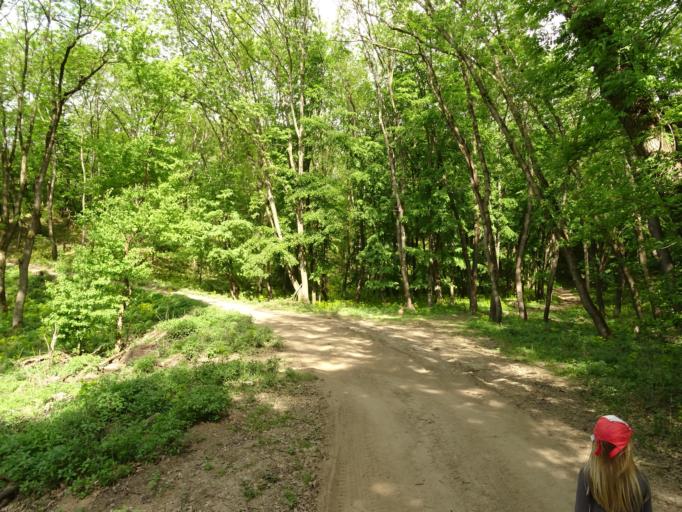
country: HU
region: Fejer
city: Szarliget
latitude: 47.4767
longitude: 18.4647
